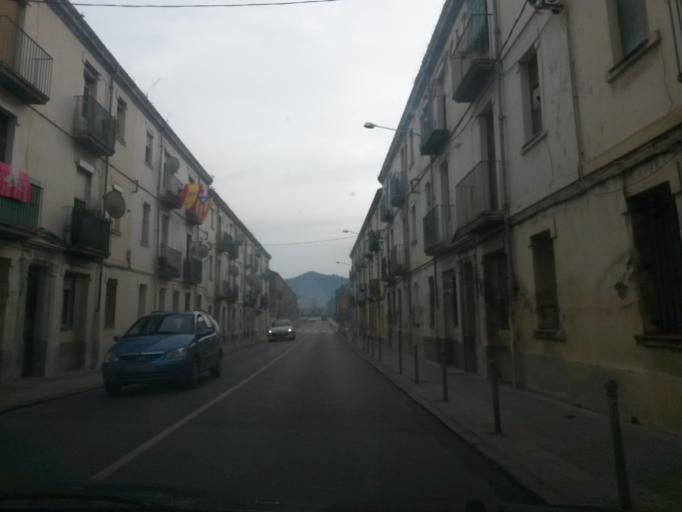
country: ES
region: Catalonia
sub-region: Provincia de Girona
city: Angles
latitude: 41.9604
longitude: 2.6324
